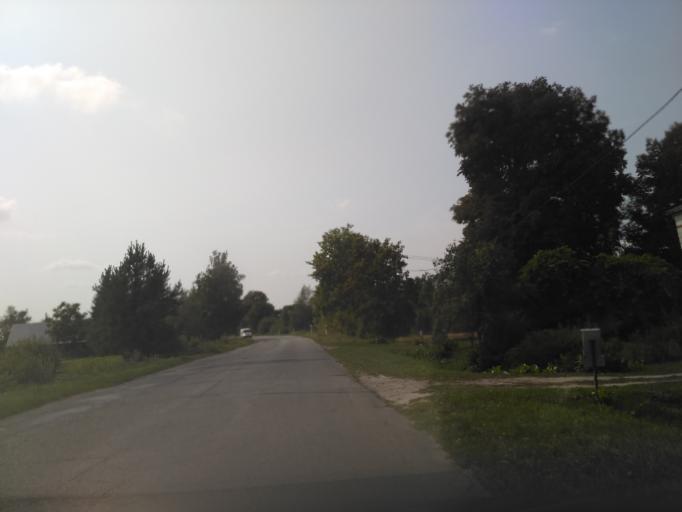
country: PL
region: Lublin Voivodeship
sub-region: Powiat wlodawski
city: Urszulin
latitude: 51.3803
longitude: 23.1727
